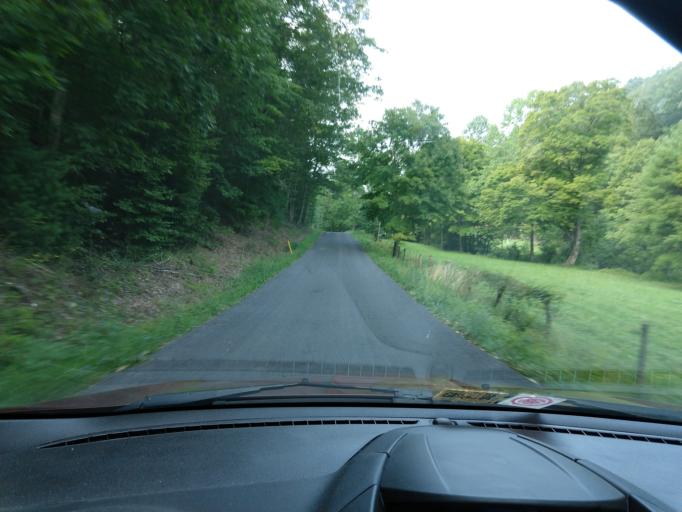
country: US
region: Virginia
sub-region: City of Covington
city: Covington
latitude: 37.9058
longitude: -80.0806
